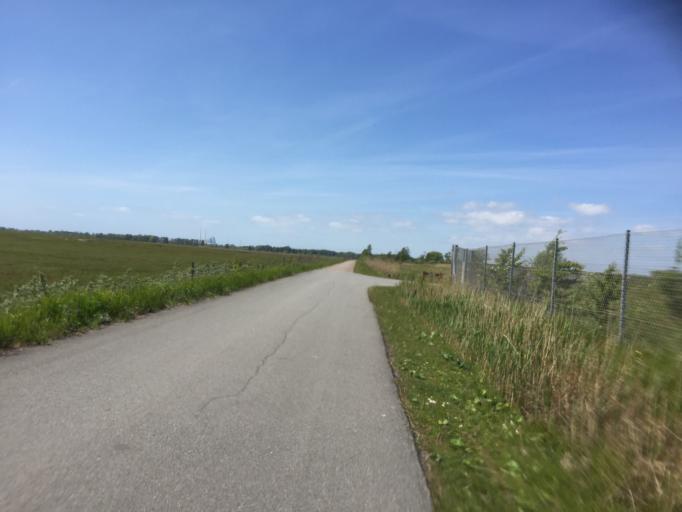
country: DK
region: Capital Region
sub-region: Tarnby Kommune
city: Tarnby
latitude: 55.6155
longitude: 12.5657
